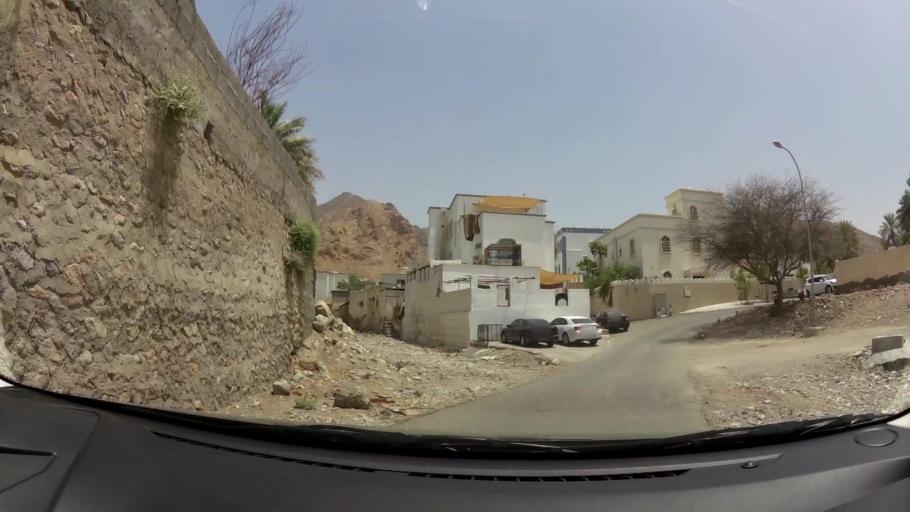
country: OM
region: Muhafazat Masqat
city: Bawshar
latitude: 23.5340
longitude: 58.3916
